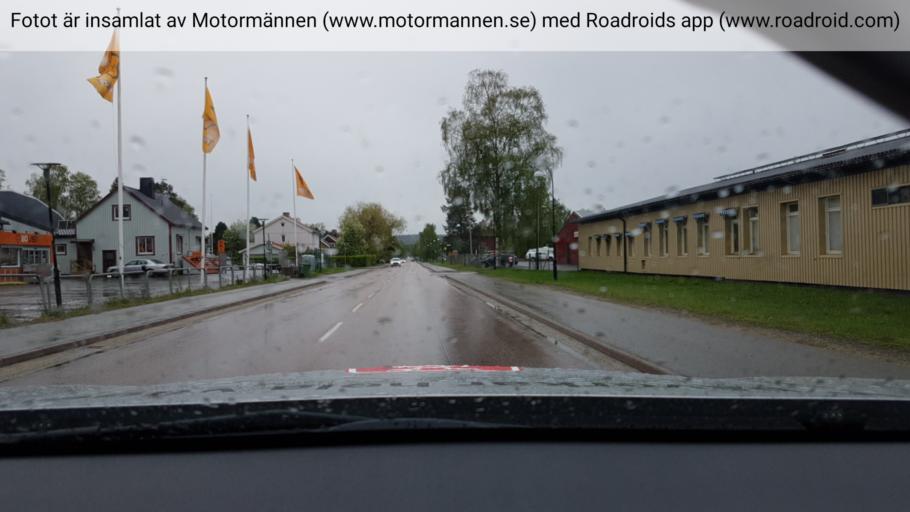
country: SE
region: Vaesterbotten
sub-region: Vannas Kommun
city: Vaennaes
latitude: 63.9119
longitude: 19.7504
